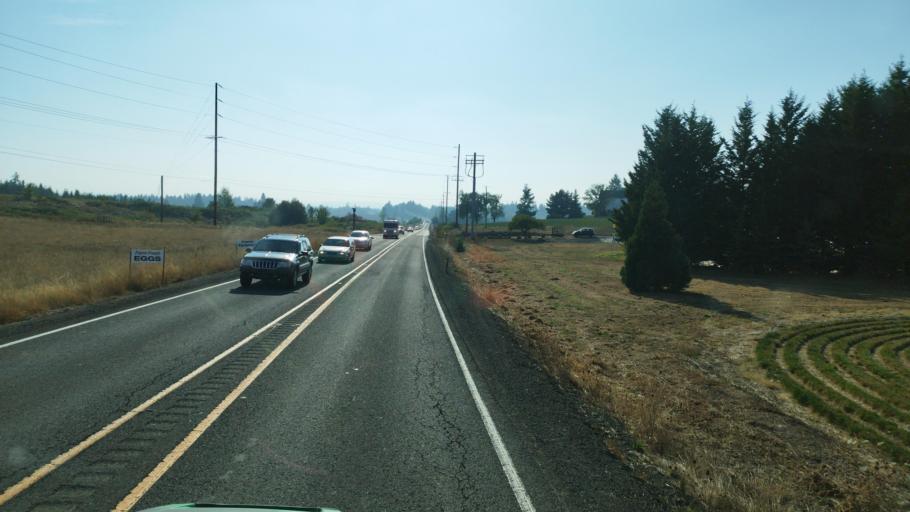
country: US
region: Oregon
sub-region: Washington County
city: Bethany
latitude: 45.5806
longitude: -122.8746
